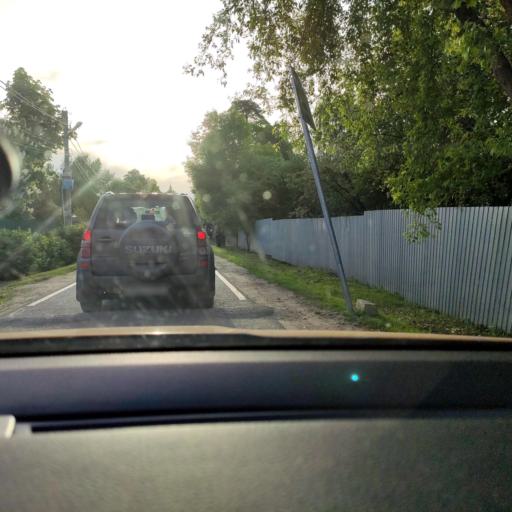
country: RU
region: Moskovskaya
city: Selyatino
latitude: 55.5285
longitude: 37.0026
